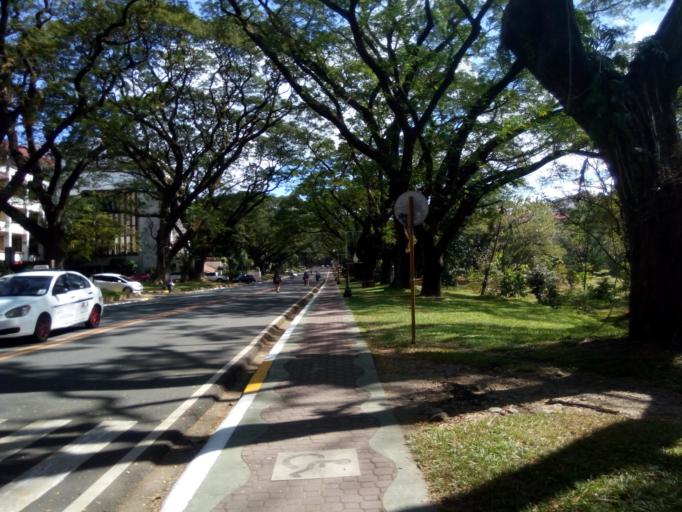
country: PH
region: Metro Manila
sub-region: Quezon City
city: Quezon City
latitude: 14.6560
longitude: 121.0686
